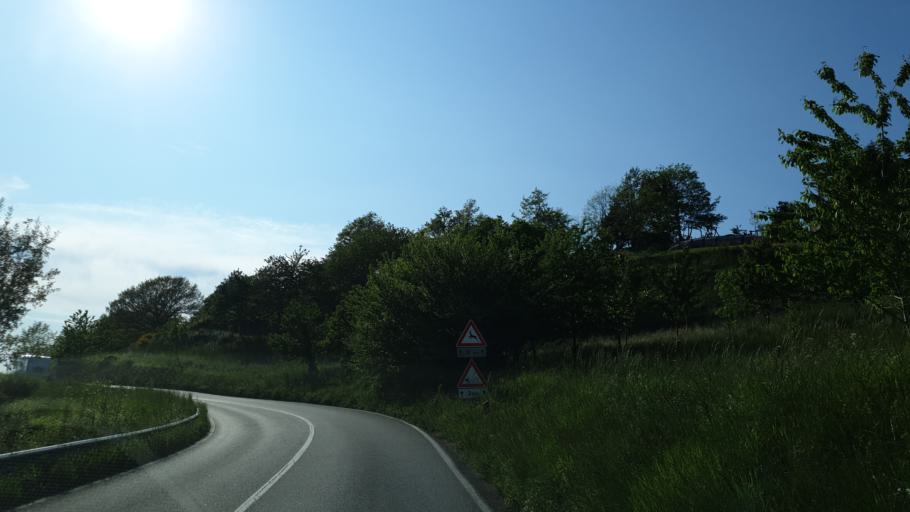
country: IT
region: Tuscany
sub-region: Province of Arezzo
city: Stia
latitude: 43.7815
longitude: 11.6608
